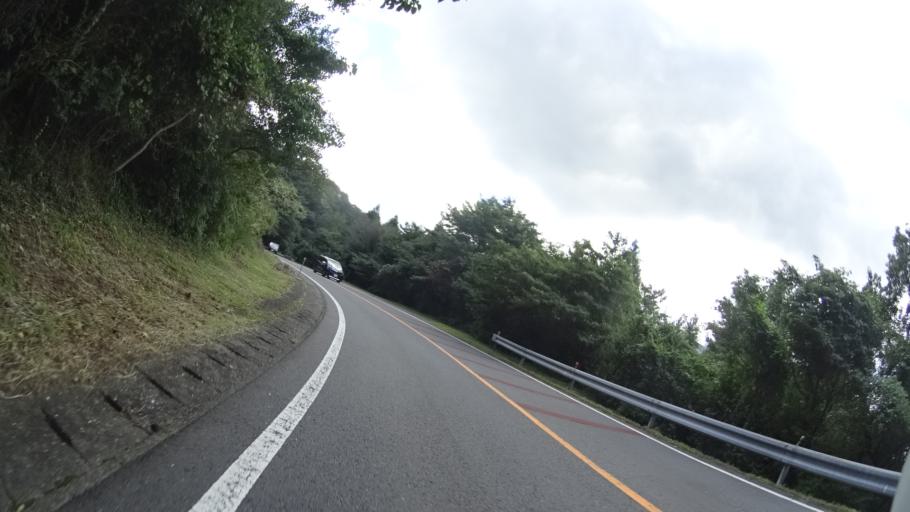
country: JP
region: Oita
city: Tsukawaki
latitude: 33.2440
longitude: 131.2839
